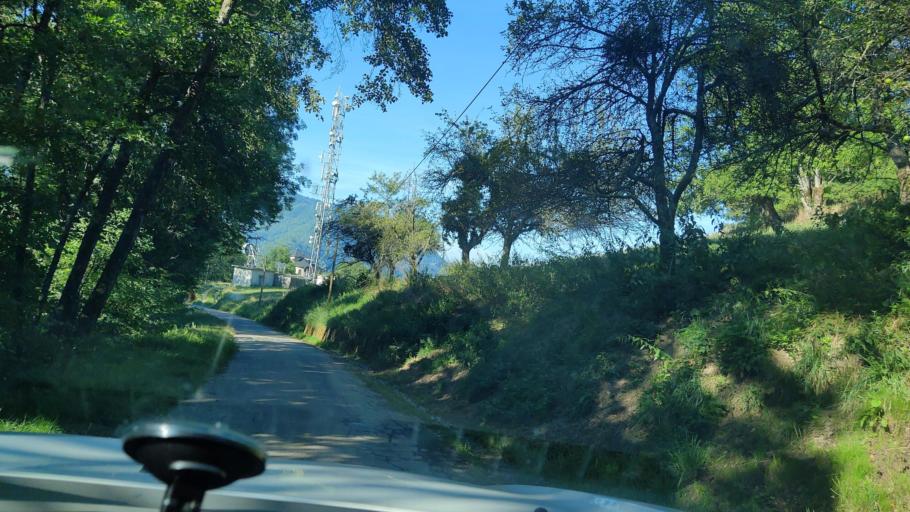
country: FR
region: Rhone-Alpes
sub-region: Departement de la Savoie
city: Aiton
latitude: 45.5641
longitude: 6.3051
